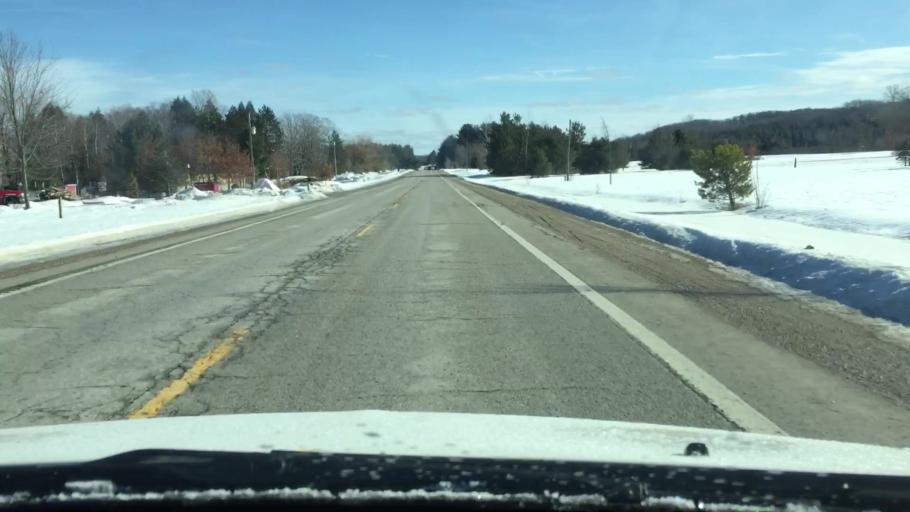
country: US
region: Michigan
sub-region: Charlevoix County
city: East Jordan
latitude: 45.1003
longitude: -85.1134
